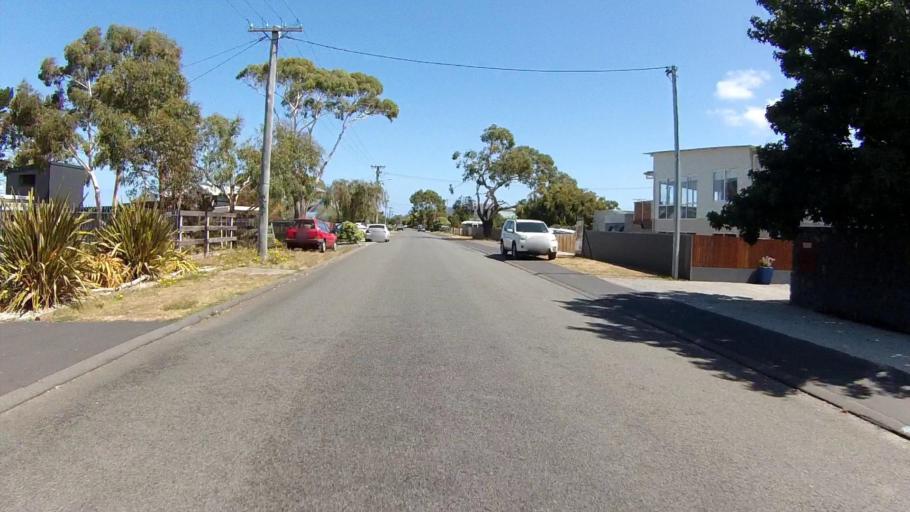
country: AU
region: Tasmania
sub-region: Clarence
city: Lauderdale
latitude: -42.8986
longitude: 147.4969
